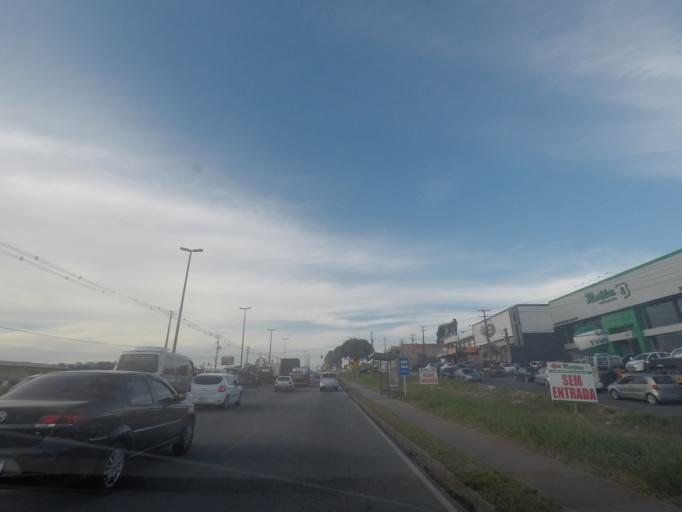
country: BR
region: Parana
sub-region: Pinhais
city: Pinhais
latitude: -25.3746
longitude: -49.1935
